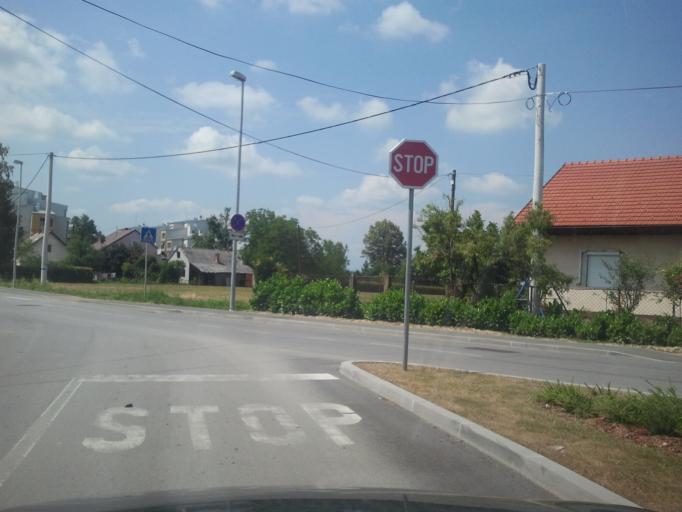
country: HR
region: Karlovacka
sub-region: Grad Karlovac
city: Karlovac
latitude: 45.4719
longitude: 15.5513
